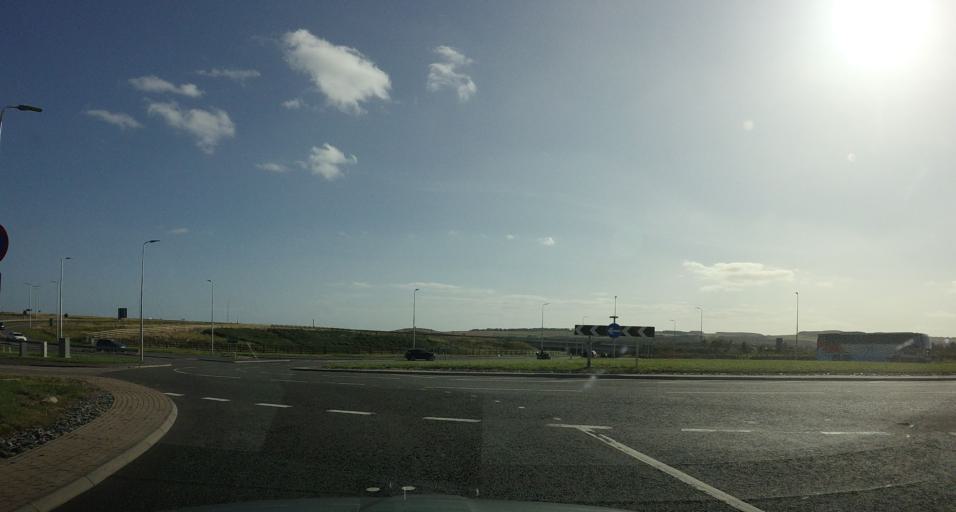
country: GB
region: Scotland
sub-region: Aberdeenshire
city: Stonehaven
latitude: 56.9785
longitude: -2.2099
